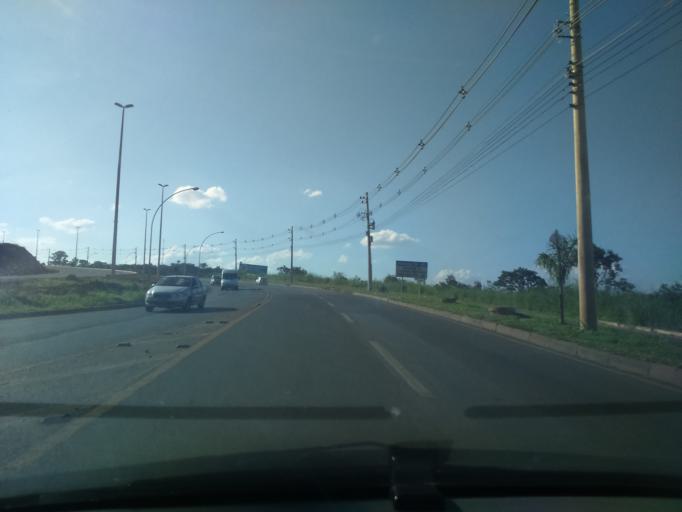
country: BR
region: Federal District
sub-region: Brasilia
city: Brasilia
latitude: -15.8949
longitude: -47.7914
